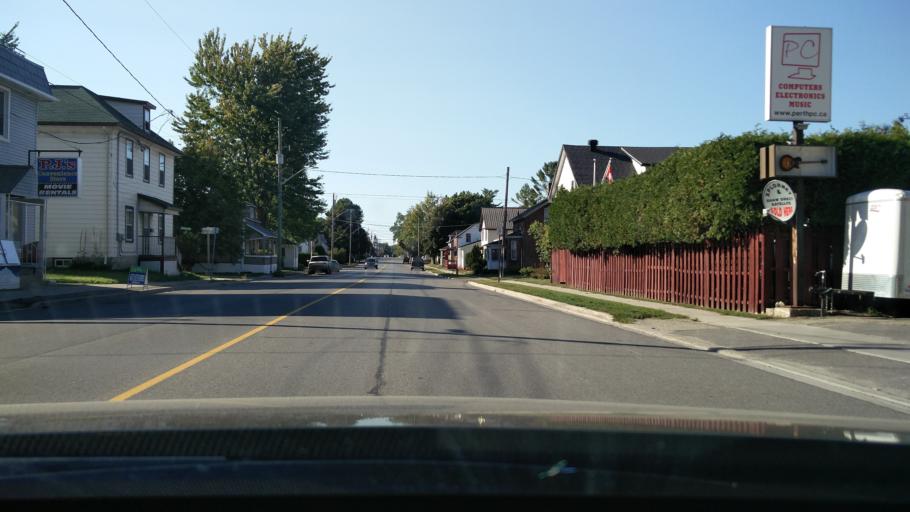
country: CA
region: Ontario
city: Perth
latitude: 44.8938
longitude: -76.2422
